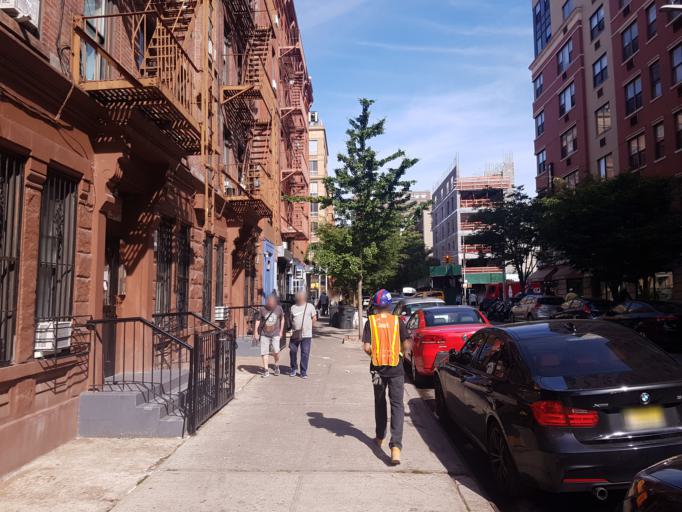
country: US
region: New York
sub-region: New York County
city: Manhattan
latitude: 40.8049
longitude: -73.9543
